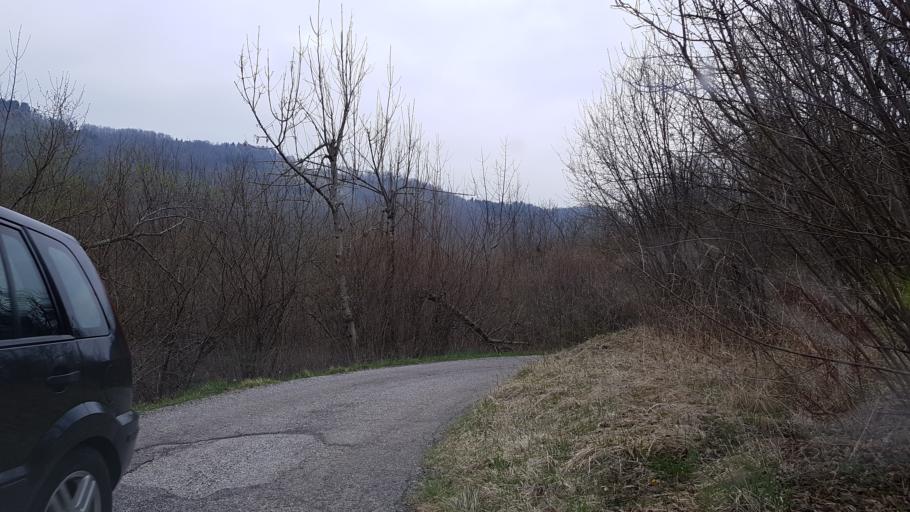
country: IT
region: Friuli Venezia Giulia
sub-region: Provincia di Udine
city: Faedis
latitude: 46.1835
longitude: 13.3962
